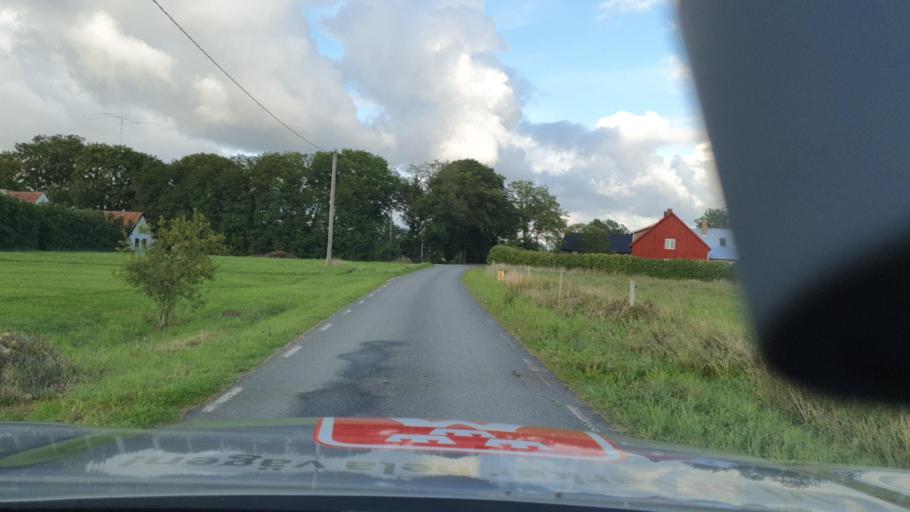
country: SE
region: Gotland
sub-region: Gotland
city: Hemse
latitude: 57.2241
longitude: 18.2397
